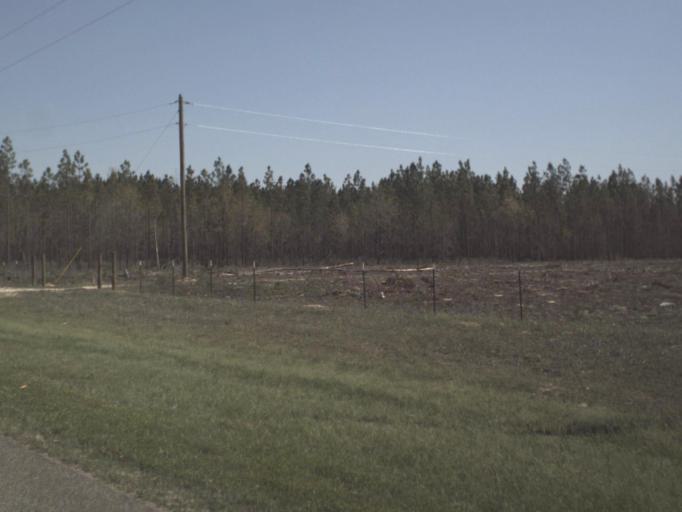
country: US
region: Florida
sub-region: Liberty County
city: Bristol
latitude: 30.4209
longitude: -84.9008
